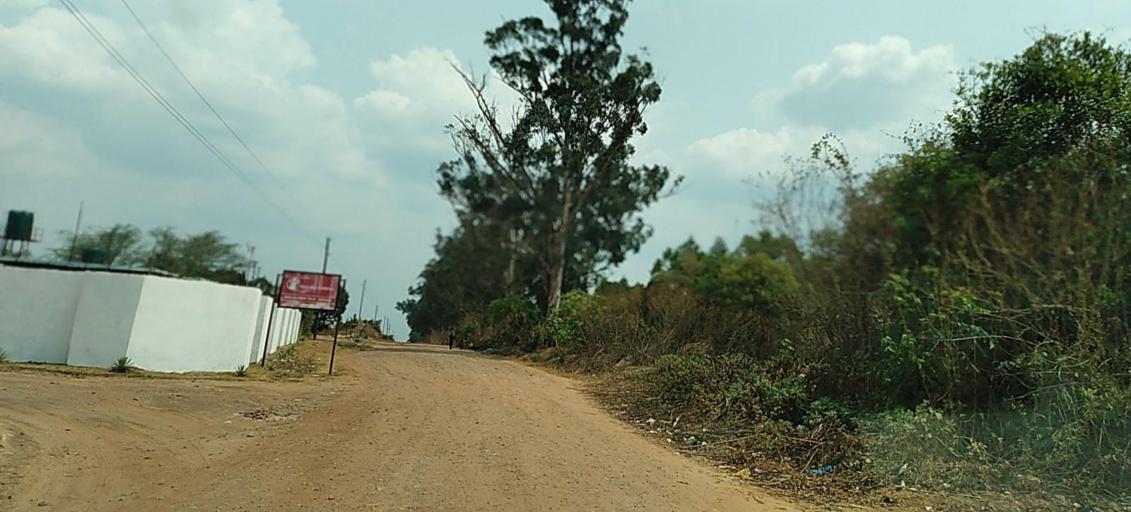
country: ZM
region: Copperbelt
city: Kalulushi
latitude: -12.8419
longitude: 28.0778
